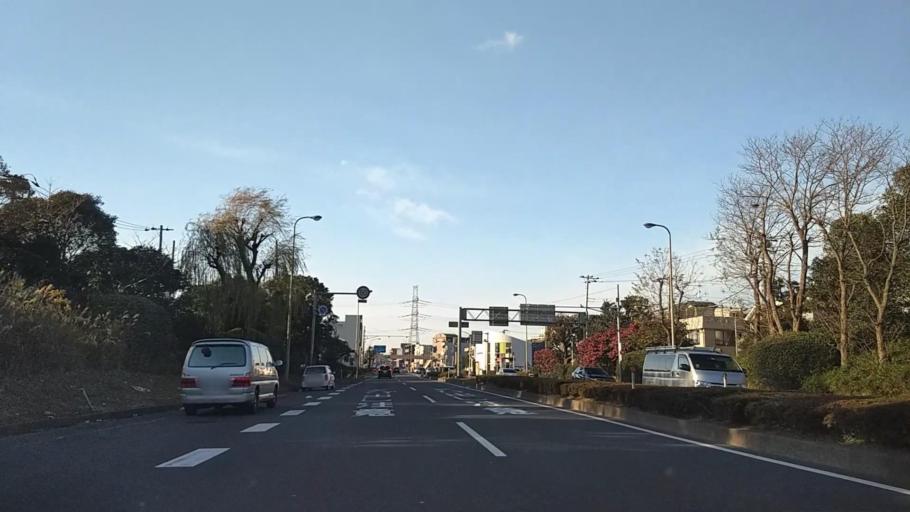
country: JP
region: Tokyo
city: Urayasu
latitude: 35.6569
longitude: 139.9066
